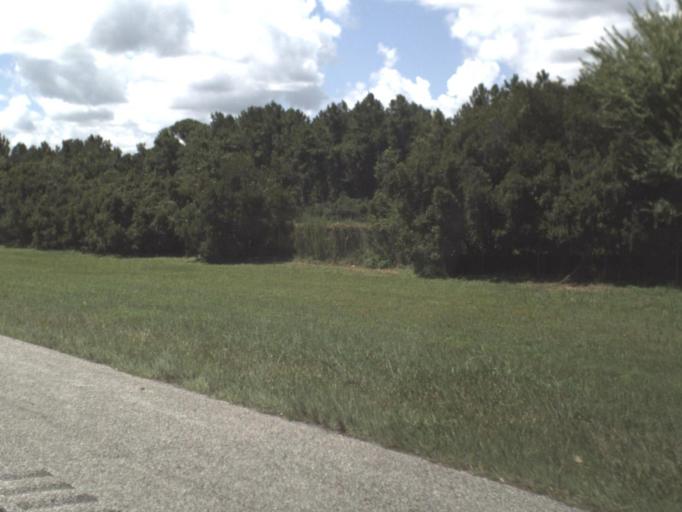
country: US
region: Florida
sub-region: Saint Johns County
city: Saint Augustine Shores
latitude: 29.7072
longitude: -81.3304
